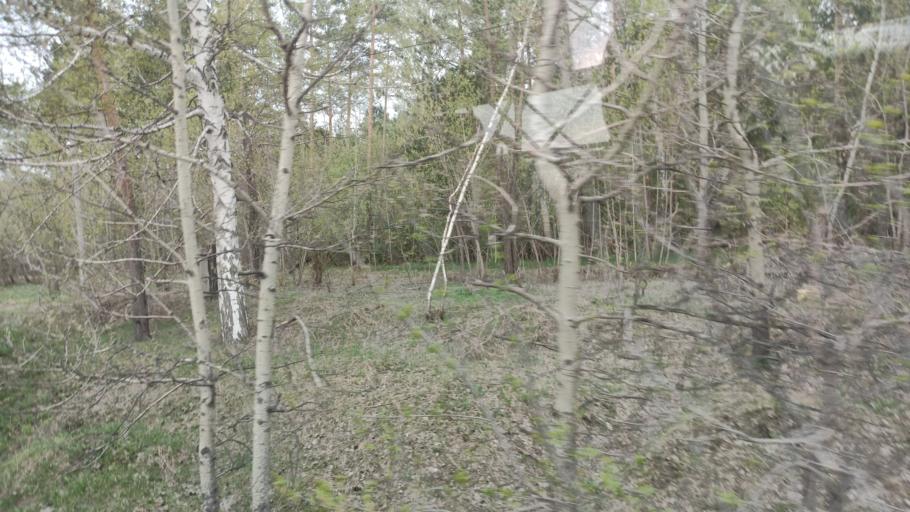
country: RU
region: Altai Krai
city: Yuzhnyy
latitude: 53.2681
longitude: 83.7248
